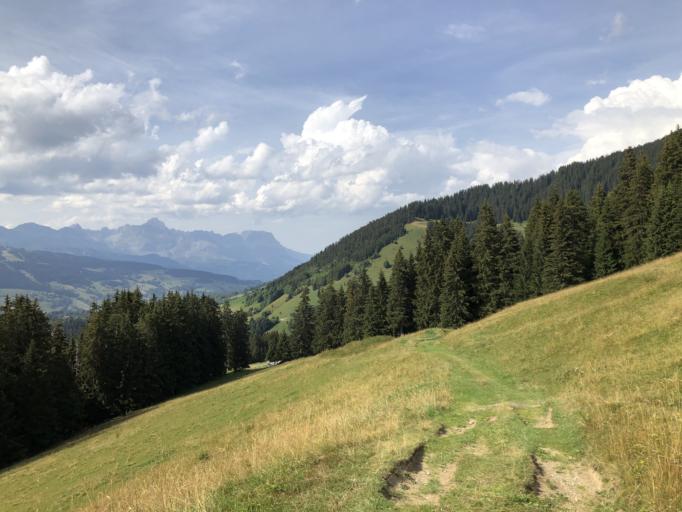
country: FR
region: Rhone-Alpes
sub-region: Departement de la Haute-Savoie
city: Megeve
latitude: 45.8259
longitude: 6.6534
